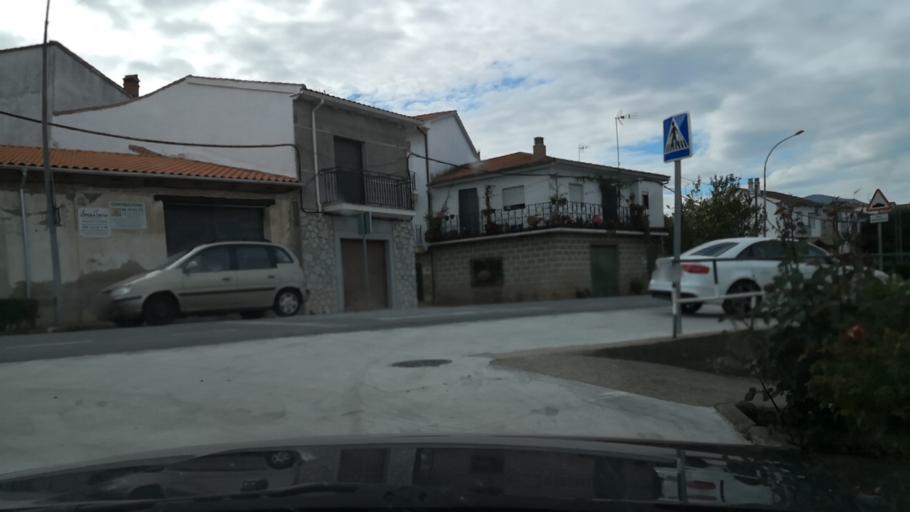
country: ES
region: Extremadura
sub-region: Provincia de Caceres
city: Perales del Puerto
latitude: 40.1571
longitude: -6.6817
